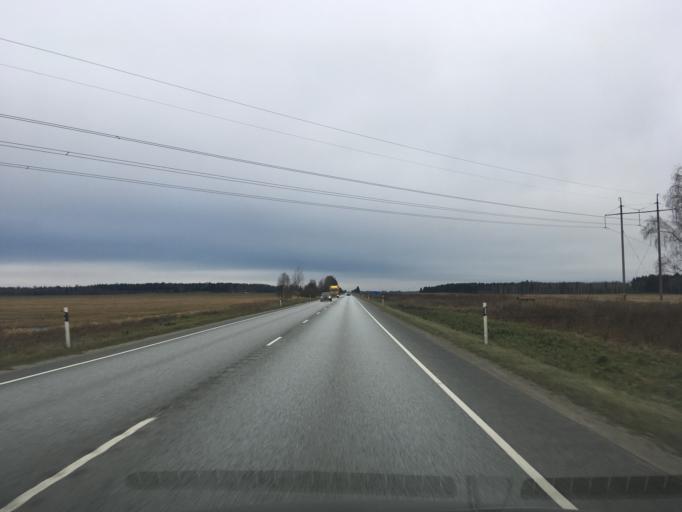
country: EE
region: Laeaene-Virumaa
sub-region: Someru vald
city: Someru
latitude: 59.3683
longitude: 26.5329
